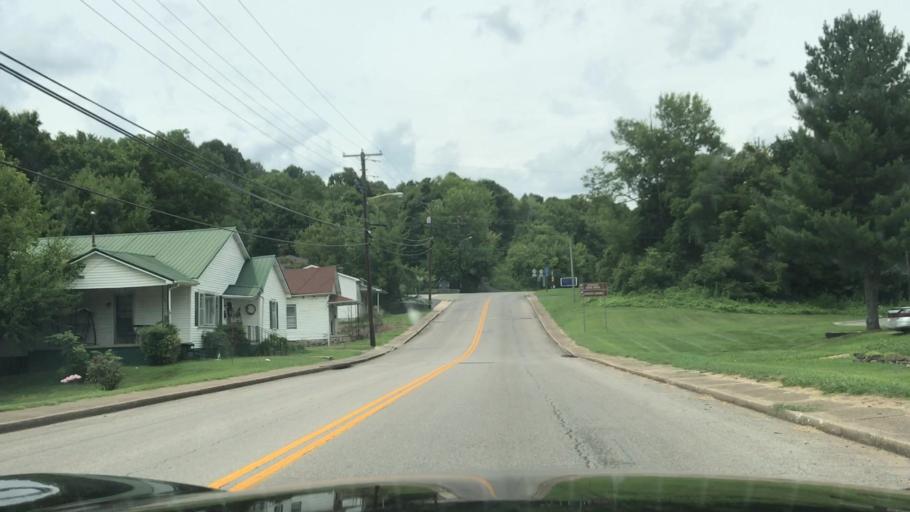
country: US
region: Kentucky
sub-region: Hart County
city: Horse Cave
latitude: 37.1800
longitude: -85.9130
